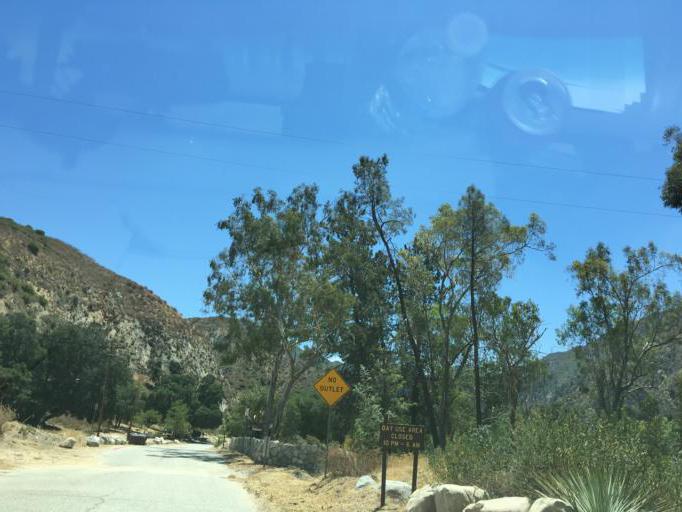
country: US
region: California
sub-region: Los Angeles County
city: La Crescenta-Montrose
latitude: 34.2857
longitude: -118.2254
